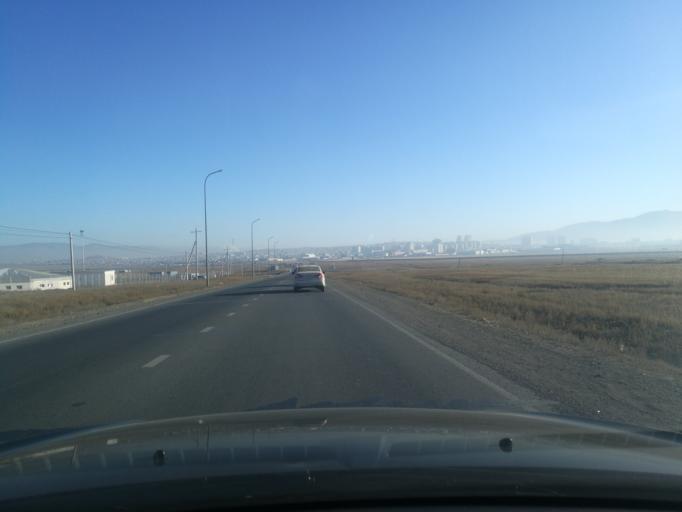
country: MN
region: Ulaanbaatar
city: Ulaanbaatar
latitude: 47.8491
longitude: 106.7380
